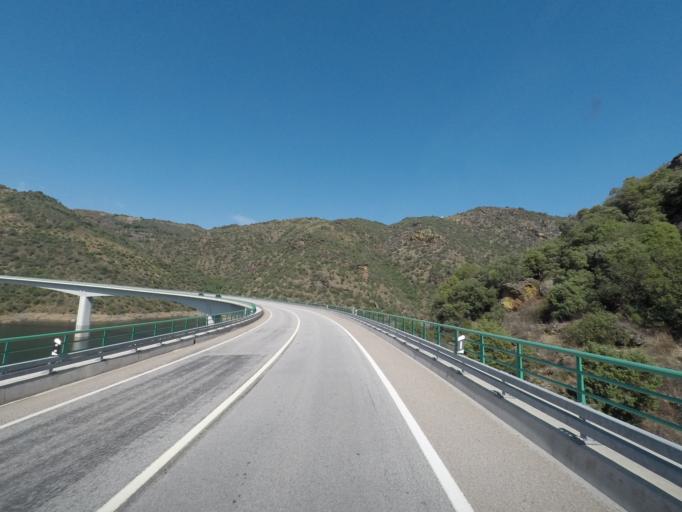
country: PT
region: Braganca
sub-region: Alfandega da Fe
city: Alfandega da Fe
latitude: 41.2862
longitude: -6.8716
